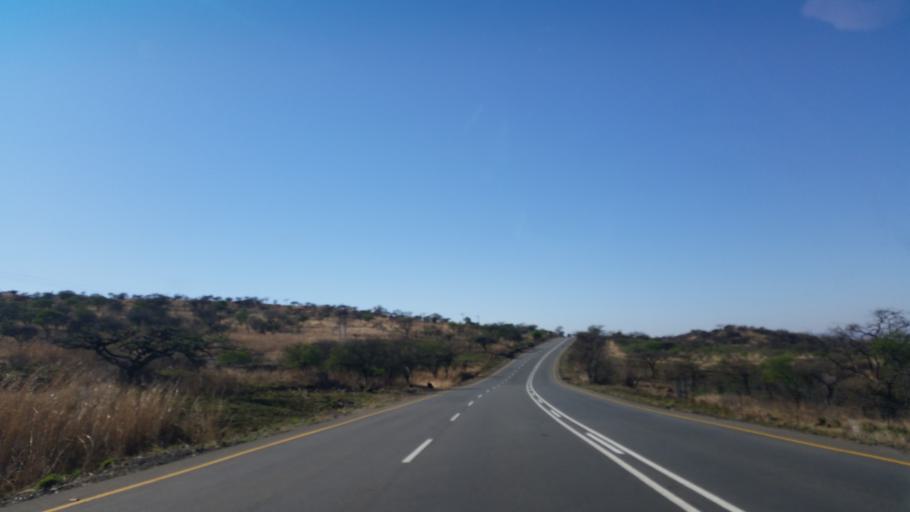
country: ZA
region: KwaZulu-Natal
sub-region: uThukela District Municipality
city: Ladysmith
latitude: -28.6920
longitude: 29.7615
